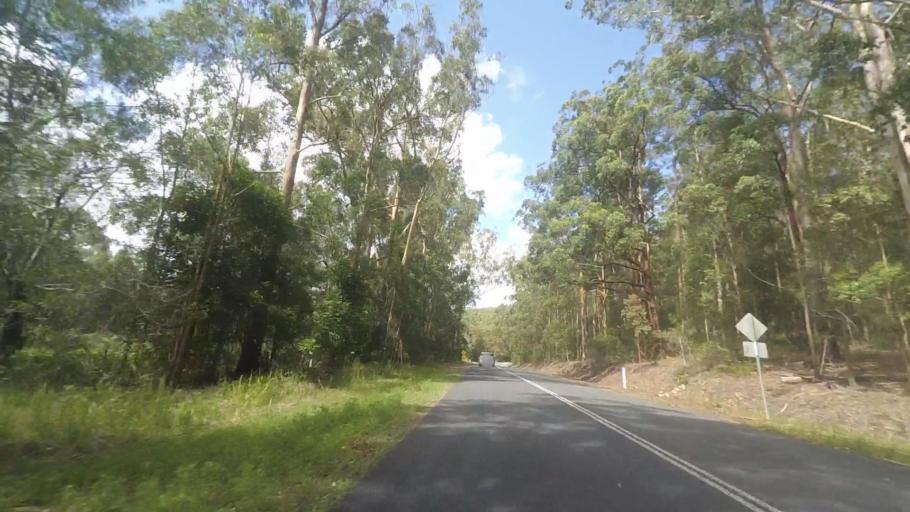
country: AU
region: New South Wales
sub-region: Great Lakes
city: Bulahdelah
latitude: -32.4002
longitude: 152.2898
